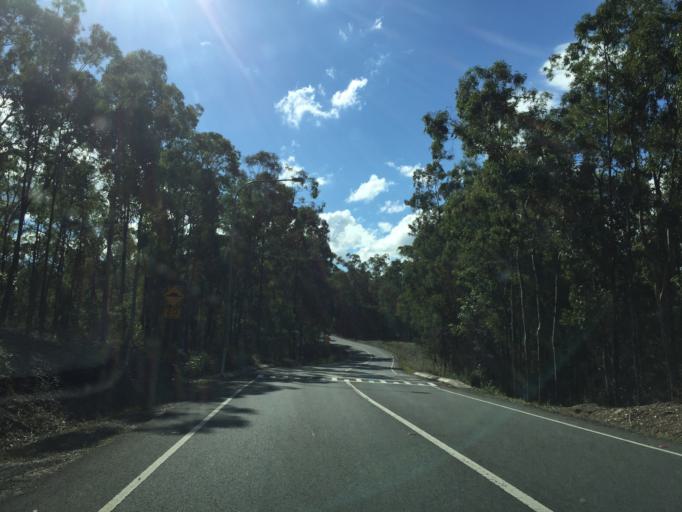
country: AU
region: Queensland
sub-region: Brisbane
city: Kenmore Hills
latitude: -27.4704
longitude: 152.9263
